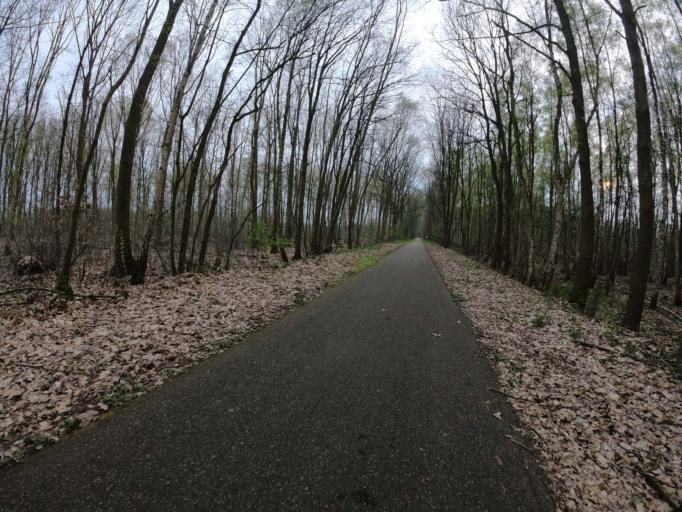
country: BE
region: Flanders
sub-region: Provincie Limburg
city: Maaseik
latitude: 51.0789
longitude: 5.7408
